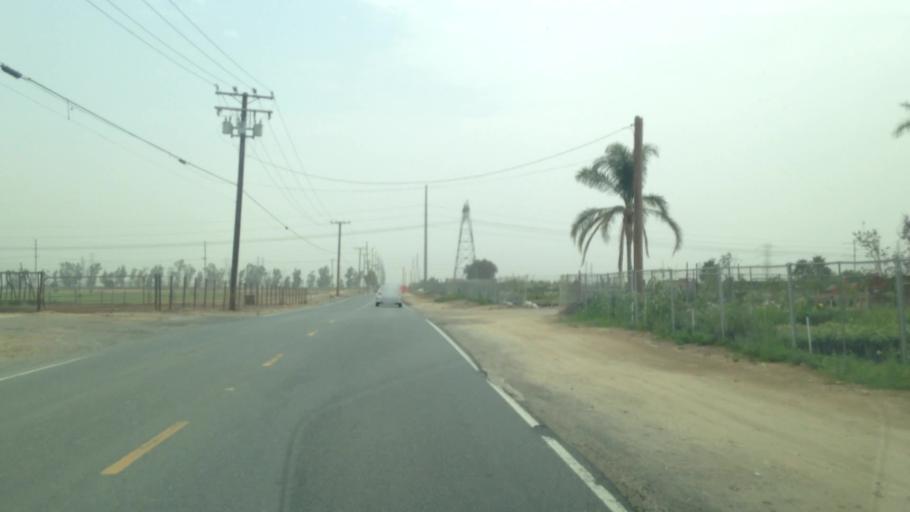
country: US
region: California
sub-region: Riverside County
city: Mira Loma
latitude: 34.0154
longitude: -117.5758
